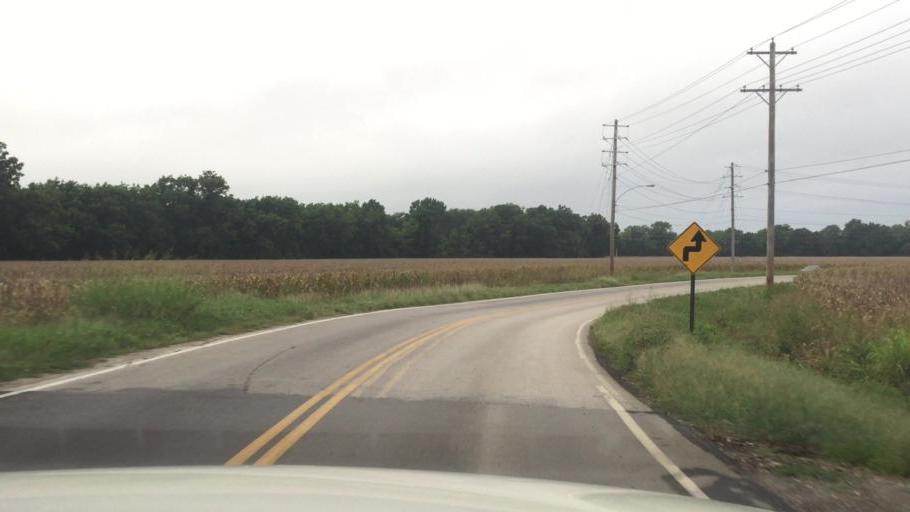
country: US
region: Kansas
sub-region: Montgomery County
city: Coffeyville
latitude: 37.0340
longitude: -95.5804
